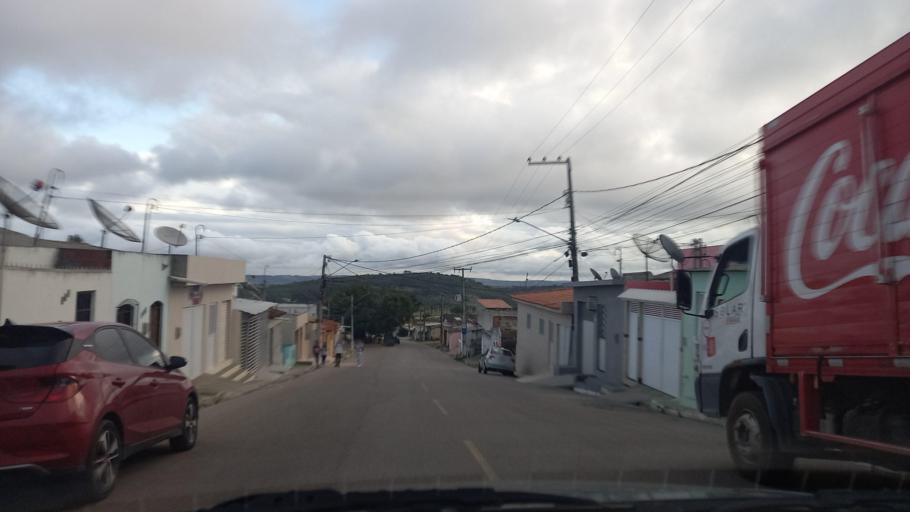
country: BR
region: Pernambuco
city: Garanhuns
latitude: -8.8831
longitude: -36.5050
